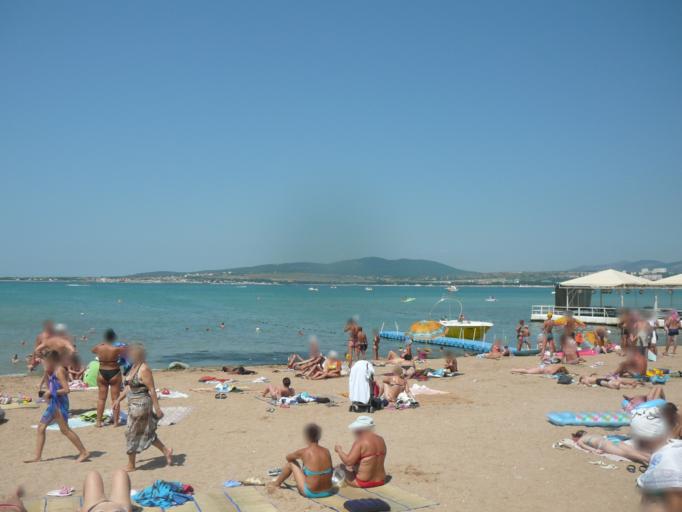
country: RU
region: Krasnodarskiy
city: Gelendzhik
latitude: 44.5625
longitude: 38.0767
